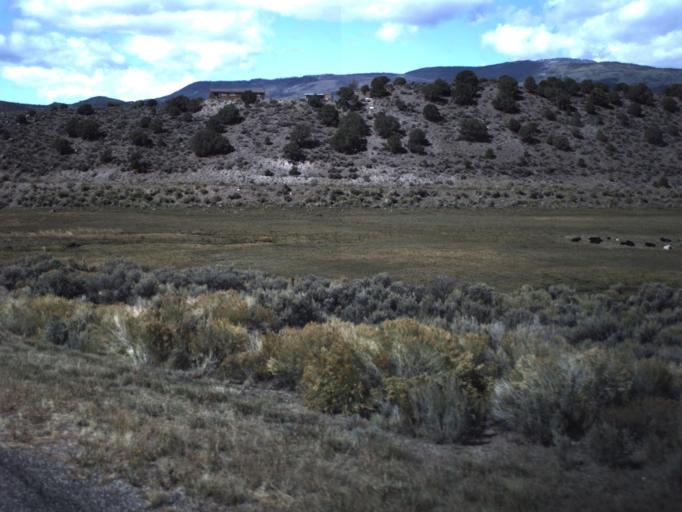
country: US
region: Utah
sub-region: Wayne County
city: Loa
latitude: 38.5651
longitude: -111.8470
